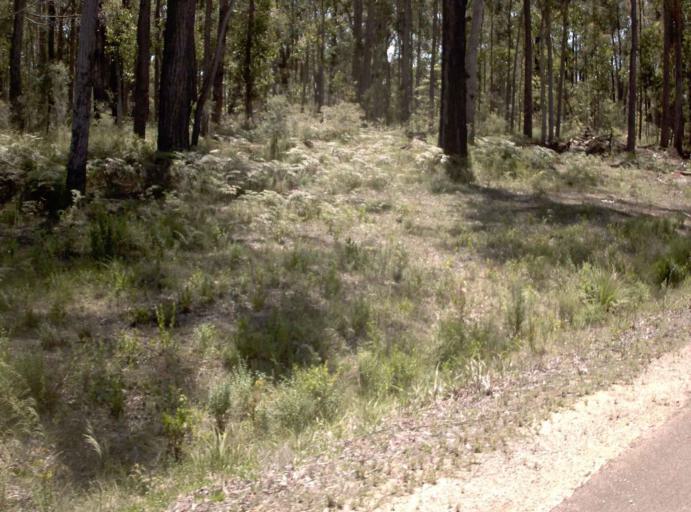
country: AU
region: Victoria
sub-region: East Gippsland
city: Lakes Entrance
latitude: -37.6655
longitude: 148.7998
